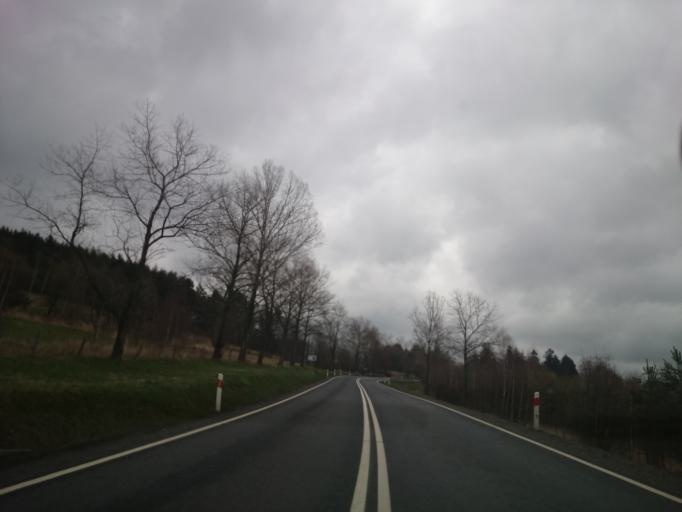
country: PL
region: Lower Silesian Voivodeship
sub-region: Powiat klodzki
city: Klodzko
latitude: 50.4342
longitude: 16.7071
